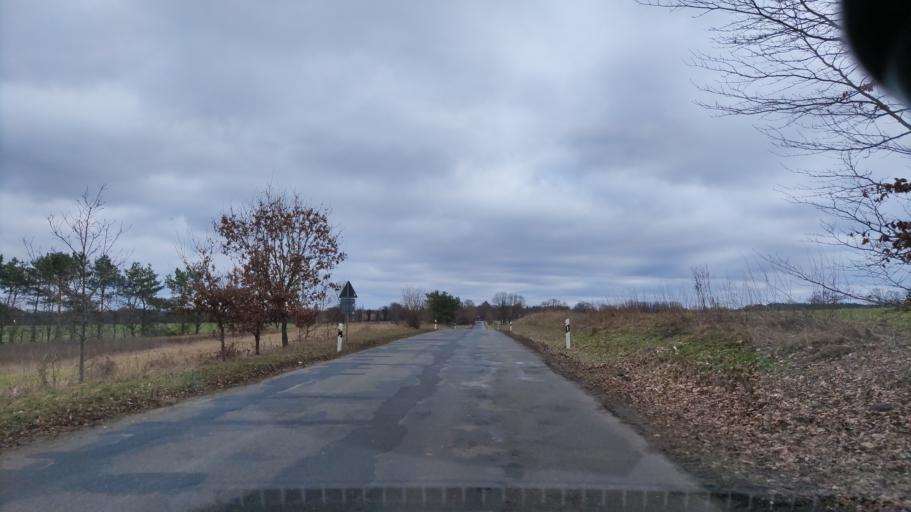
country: DE
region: Lower Saxony
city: Bleckede
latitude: 53.2647
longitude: 10.7310
